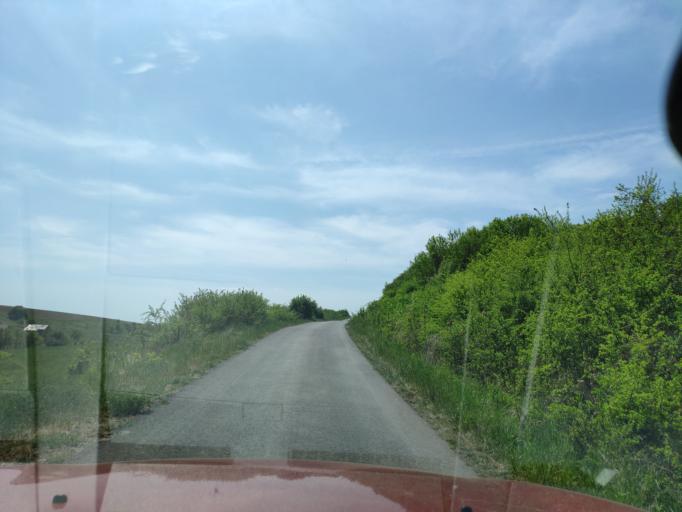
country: SK
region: Banskobystricky
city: Rimavska Sobota
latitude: 48.4214
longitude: 20.1616
